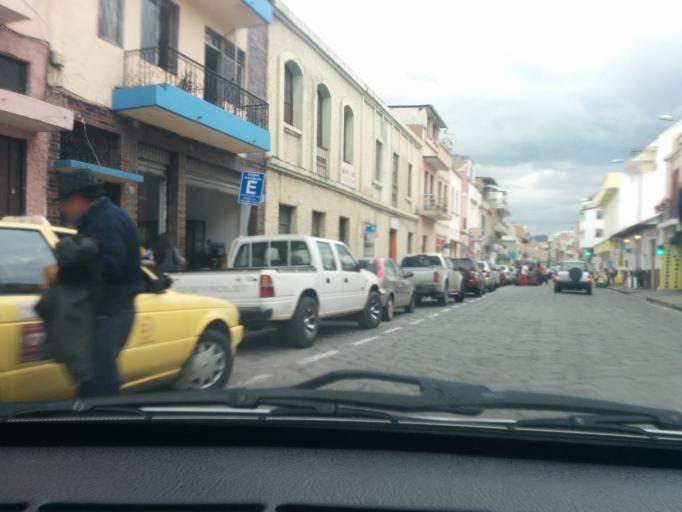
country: EC
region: Azuay
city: Cuenca
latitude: -2.8983
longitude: -78.9979
